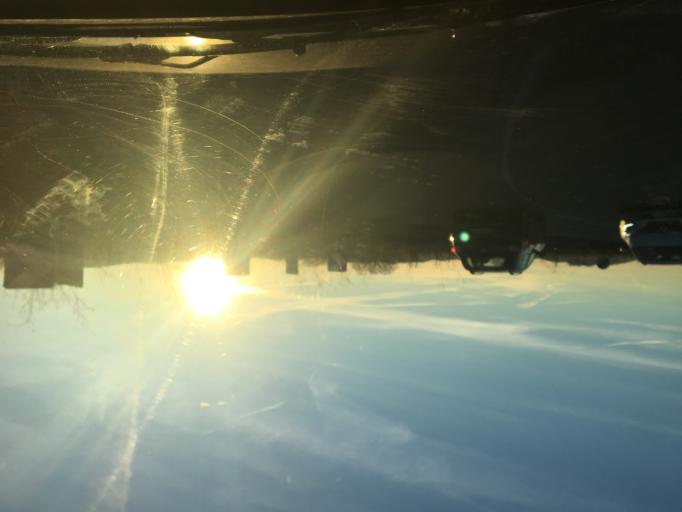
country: FR
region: Provence-Alpes-Cote d'Azur
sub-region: Departement du Var
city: Taradeau
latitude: 43.4496
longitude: 6.4496
